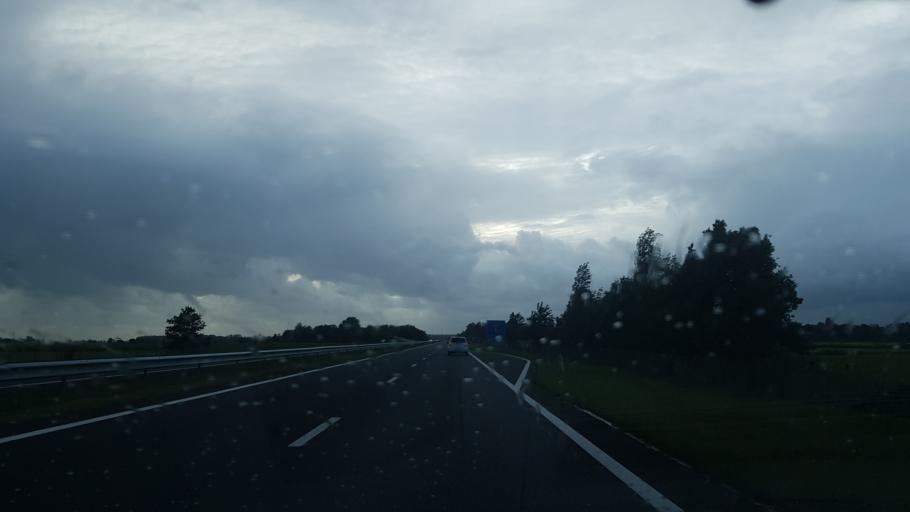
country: NL
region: Friesland
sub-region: Gemeente Tytsjerksteradiel
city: Garyp
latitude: 53.1573
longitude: 5.9619
